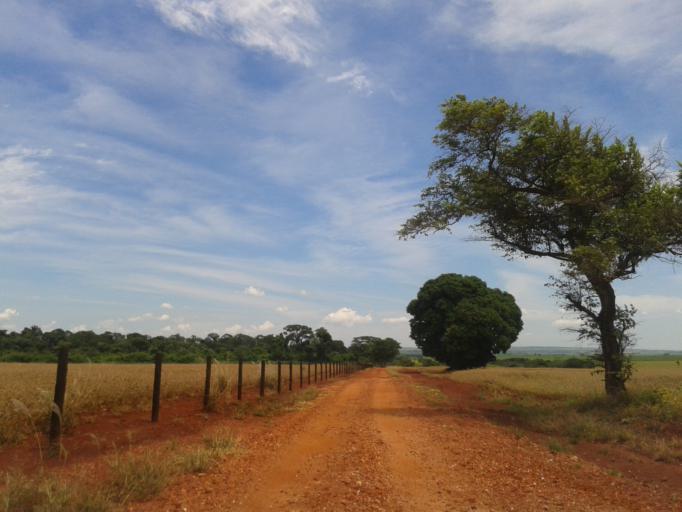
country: BR
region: Minas Gerais
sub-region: Capinopolis
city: Capinopolis
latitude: -18.6643
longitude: -49.7293
